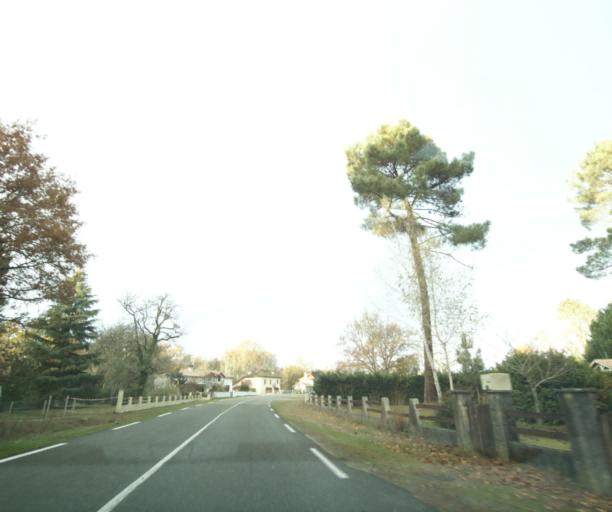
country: FR
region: Aquitaine
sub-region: Departement des Landes
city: Gabarret
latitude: 44.1025
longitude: -0.1047
